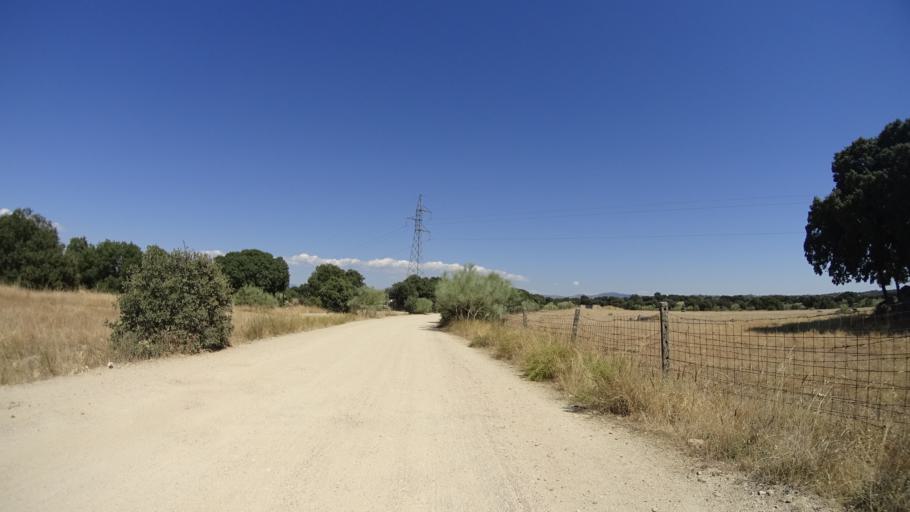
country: ES
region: Madrid
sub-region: Provincia de Madrid
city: Colmenarejo
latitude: 40.5360
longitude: -4.0106
